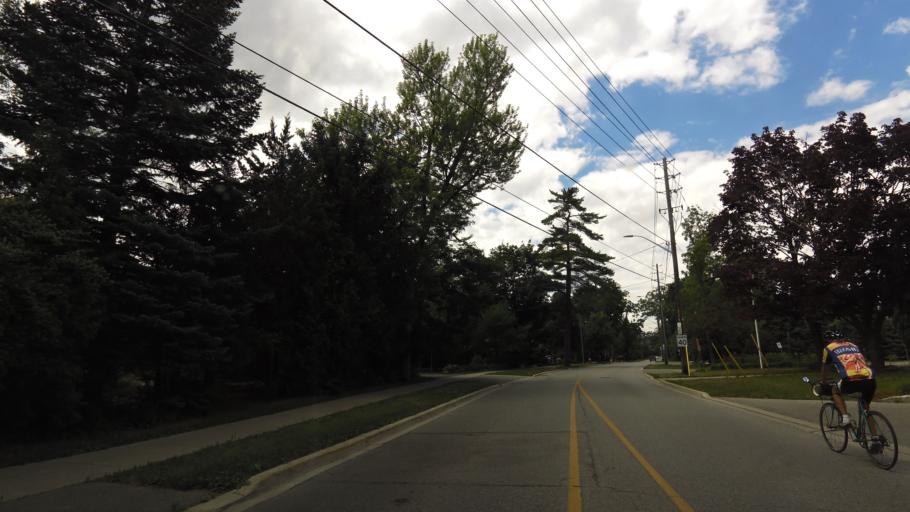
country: CA
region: Ontario
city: Mississauga
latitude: 43.5203
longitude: -79.6278
